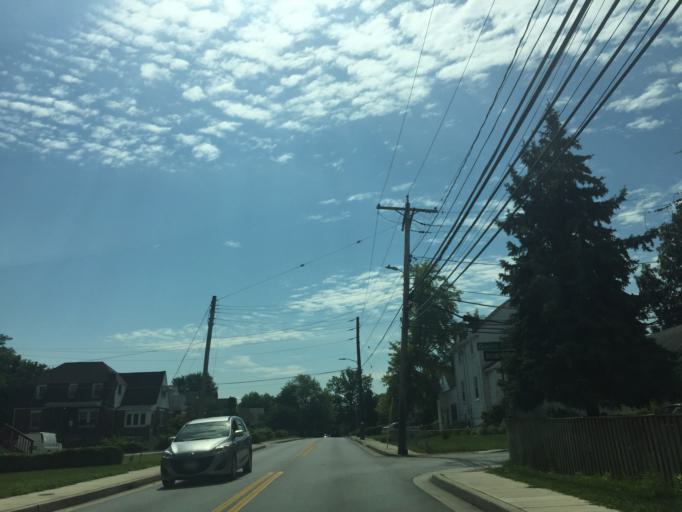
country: US
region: Maryland
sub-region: Baltimore County
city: Parkville
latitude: 39.3787
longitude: -76.5529
